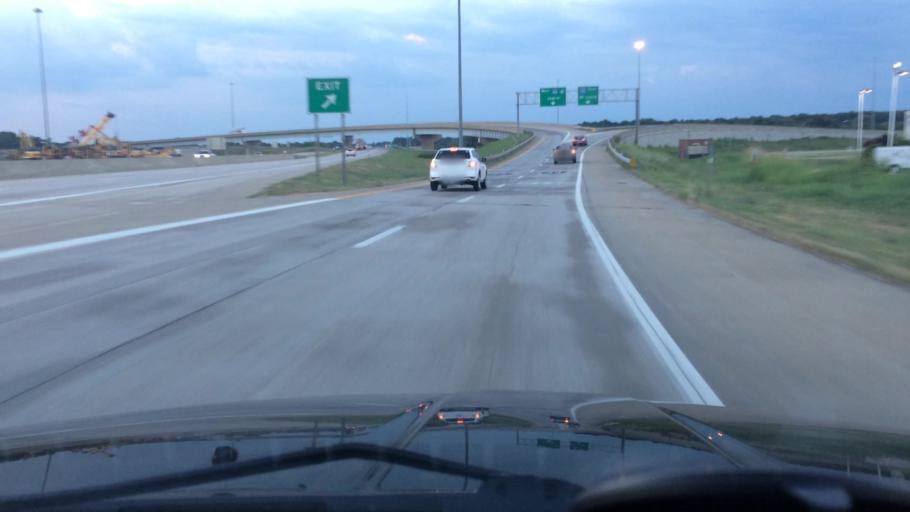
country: US
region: Missouri
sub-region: Greene County
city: Springfield
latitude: 37.2465
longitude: -93.2243
